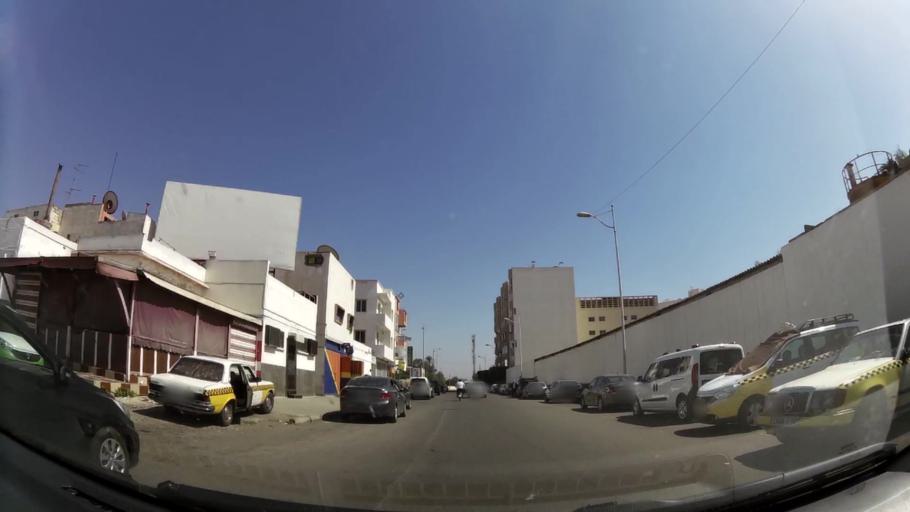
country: MA
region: Souss-Massa-Draa
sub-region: Agadir-Ida-ou-Tnan
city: Agadir
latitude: 30.4095
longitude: -9.5877
